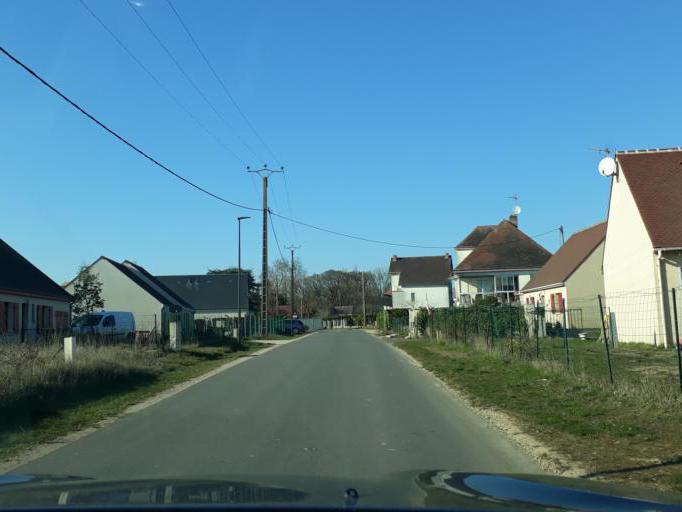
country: FR
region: Centre
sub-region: Departement du Loir-et-Cher
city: Oucques
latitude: 47.8212
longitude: 1.4001
